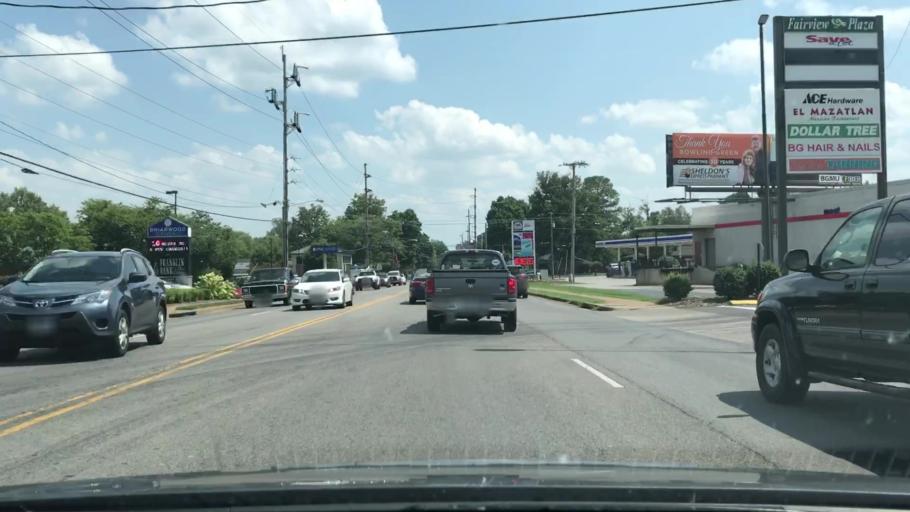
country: US
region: Kentucky
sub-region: Warren County
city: Bowling Green
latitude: 36.9907
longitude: -86.4272
